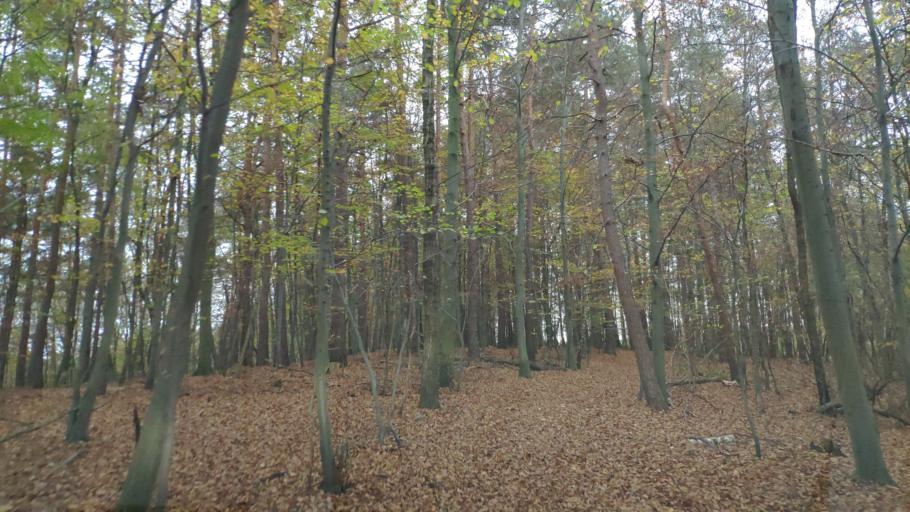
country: SK
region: Presovsky
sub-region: Okres Presov
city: Presov
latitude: 48.9396
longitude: 21.1028
